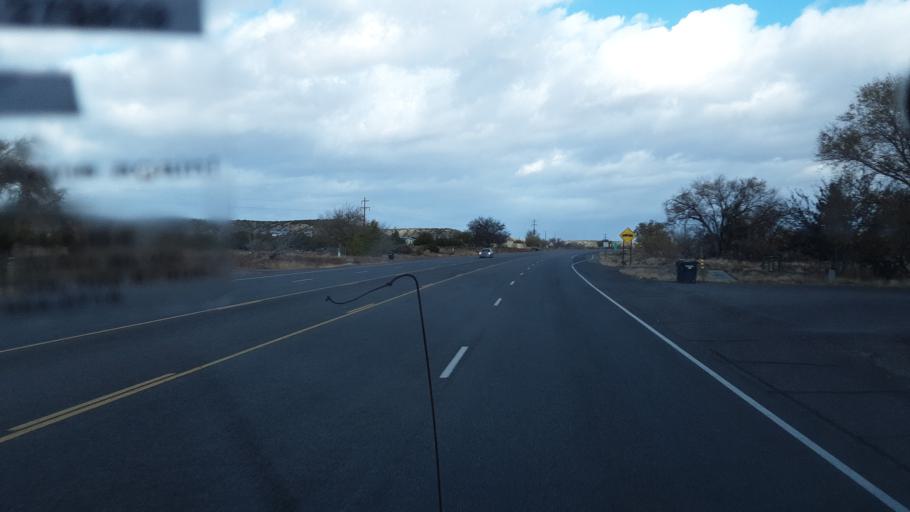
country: US
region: New Mexico
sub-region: Rio Arriba County
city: Ohkay Owingeh
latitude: 36.0501
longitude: -106.1126
